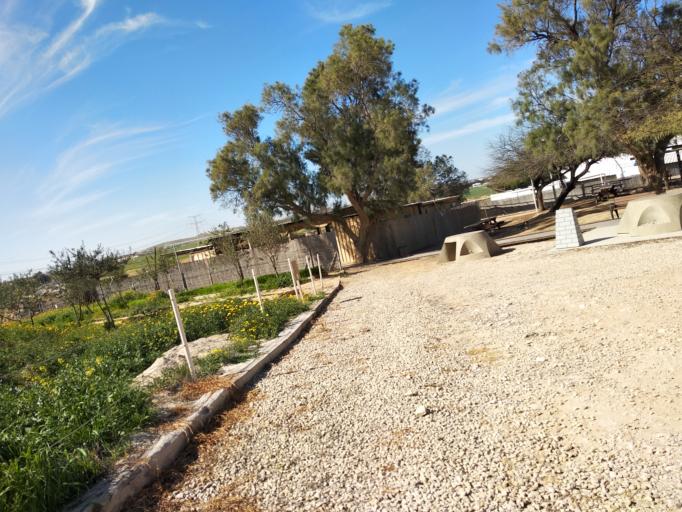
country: IL
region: Southern District
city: Beersheba
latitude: 31.2456
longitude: 34.8415
